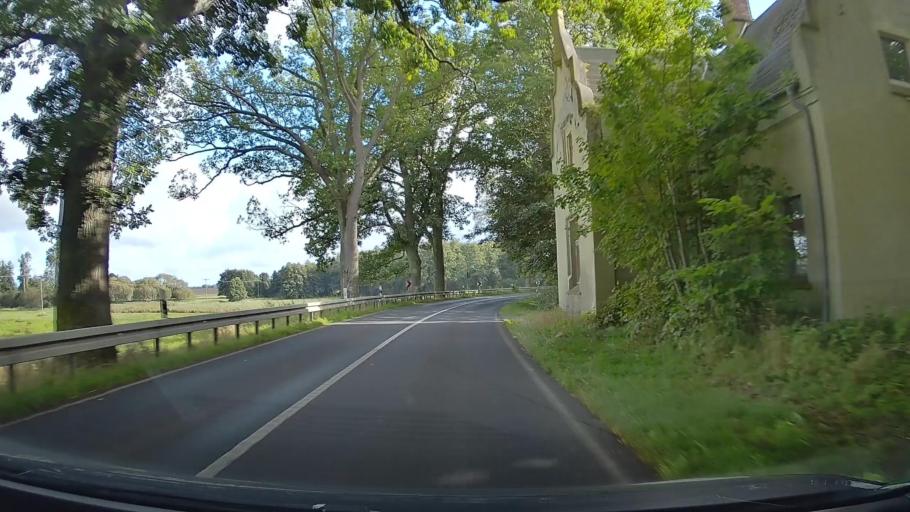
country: DE
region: Mecklenburg-Vorpommern
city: Putbus
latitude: 54.3810
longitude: 13.4797
